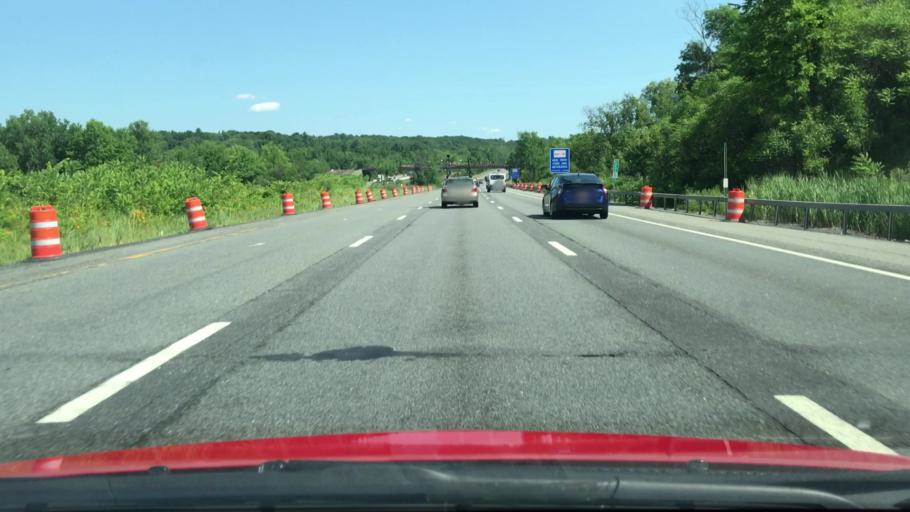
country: US
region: New York
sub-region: Saratoga County
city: Ballston Spa
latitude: 42.9914
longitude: -73.8034
